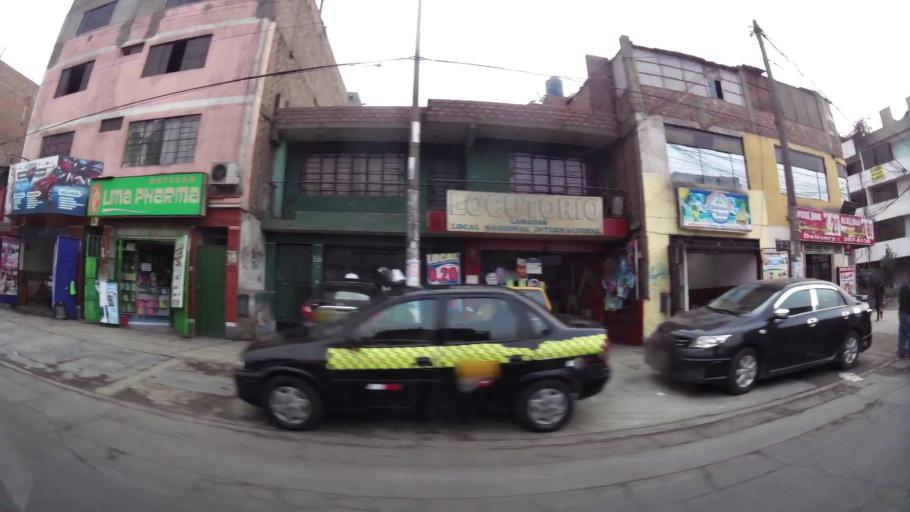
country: PE
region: Lima
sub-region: Lima
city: Independencia
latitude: -12.0007
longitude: -77.0044
